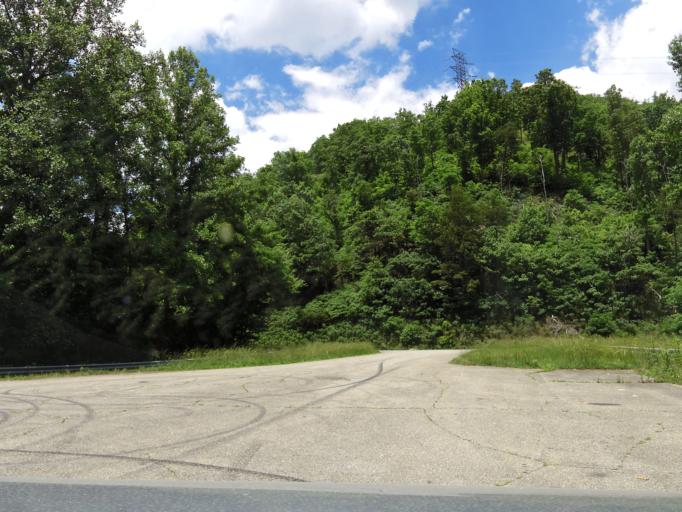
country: US
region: North Carolina
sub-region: Graham County
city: Robbinsville
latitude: 35.3662
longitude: -83.8605
